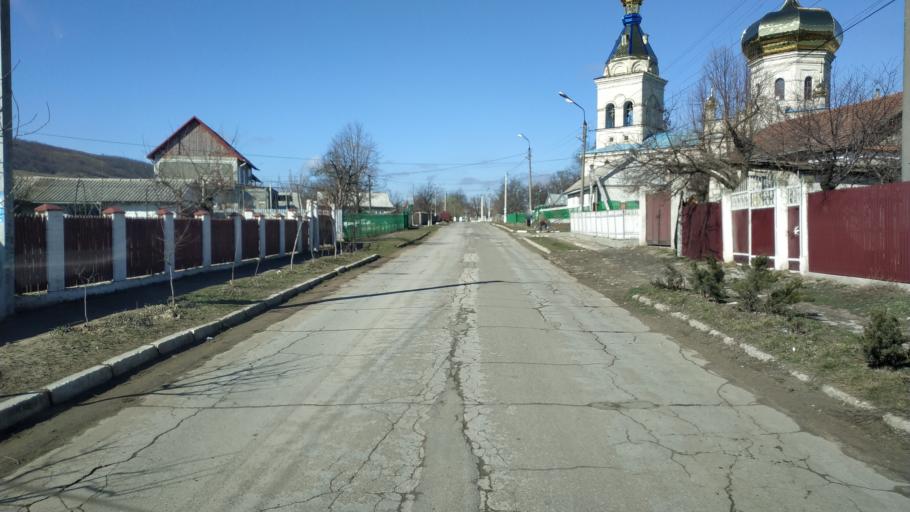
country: MD
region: Hincesti
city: Hincesti
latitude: 46.9721
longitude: 28.5815
